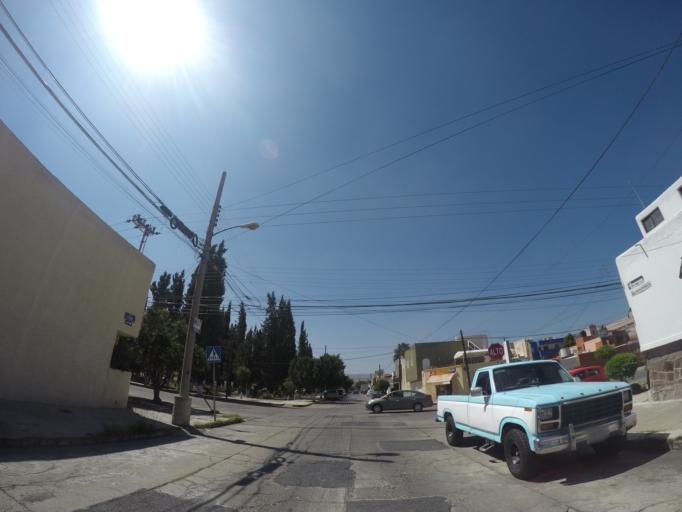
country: MX
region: San Luis Potosi
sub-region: San Luis Potosi
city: San Luis Potosi
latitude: 22.1447
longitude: -101.0114
